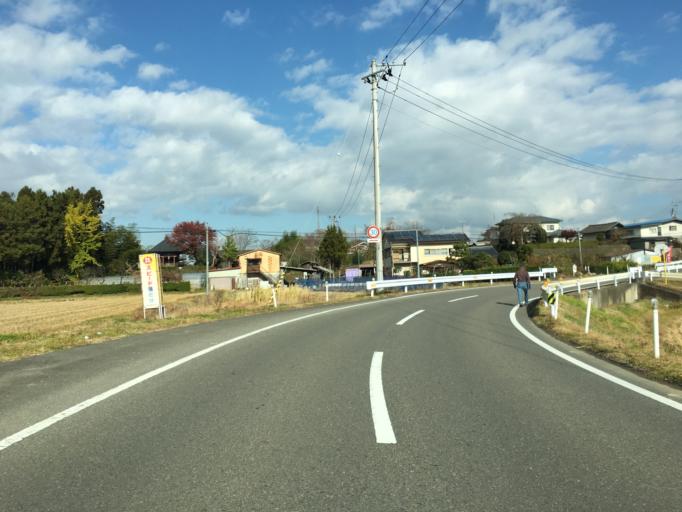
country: JP
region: Fukushima
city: Nihommatsu
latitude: 37.6480
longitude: 140.4817
